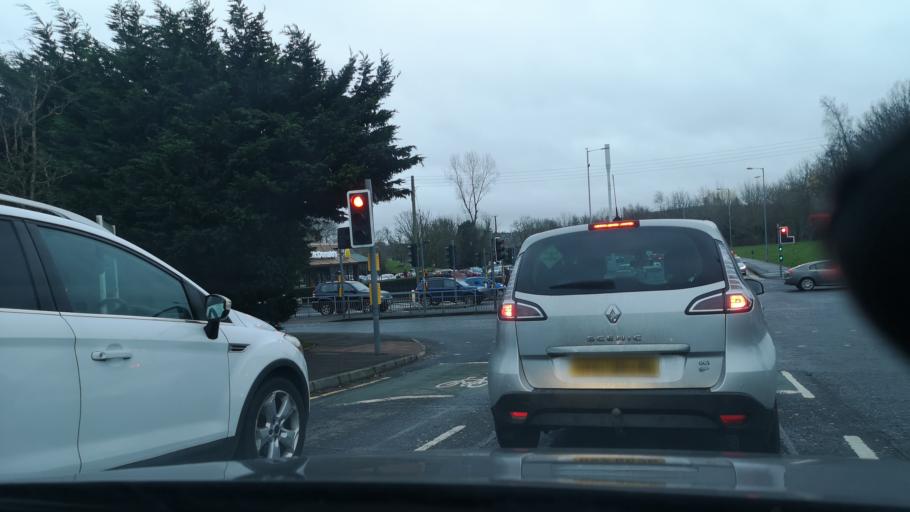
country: GB
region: Northern Ireland
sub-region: Castlereagh District
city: Dundonald
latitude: 54.5952
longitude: -5.8095
